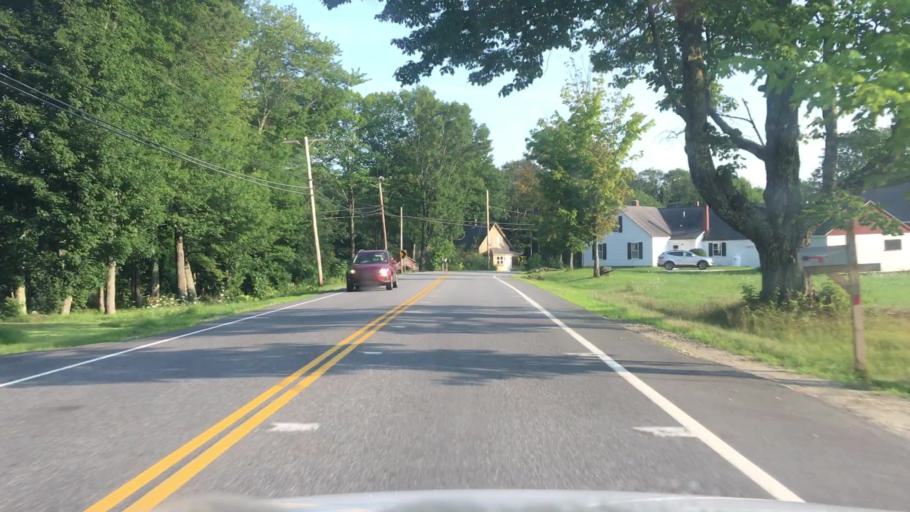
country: US
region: Maine
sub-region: Cumberland County
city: Freeport
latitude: 43.8825
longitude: -70.0930
